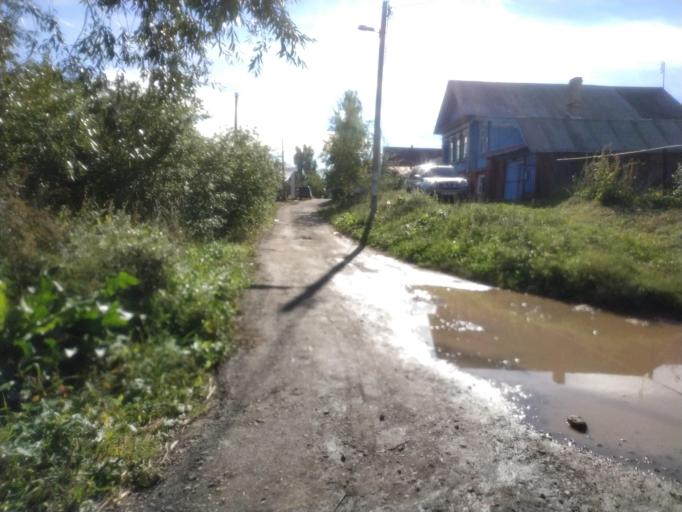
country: RU
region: Chuvashia
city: Novyye Lapsary
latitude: 56.1472
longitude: 47.1509
